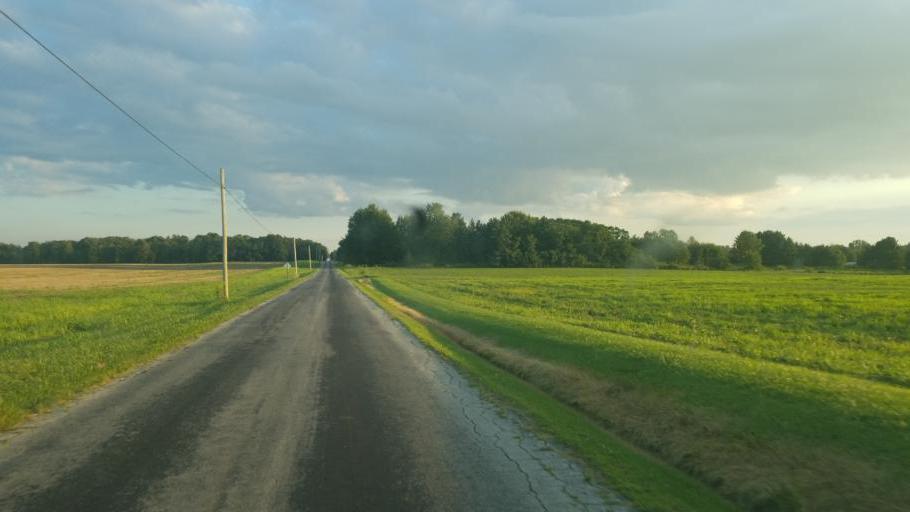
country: US
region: Ohio
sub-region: Richland County
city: Lincoln Heights
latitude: 40.8793
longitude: -82.5328
